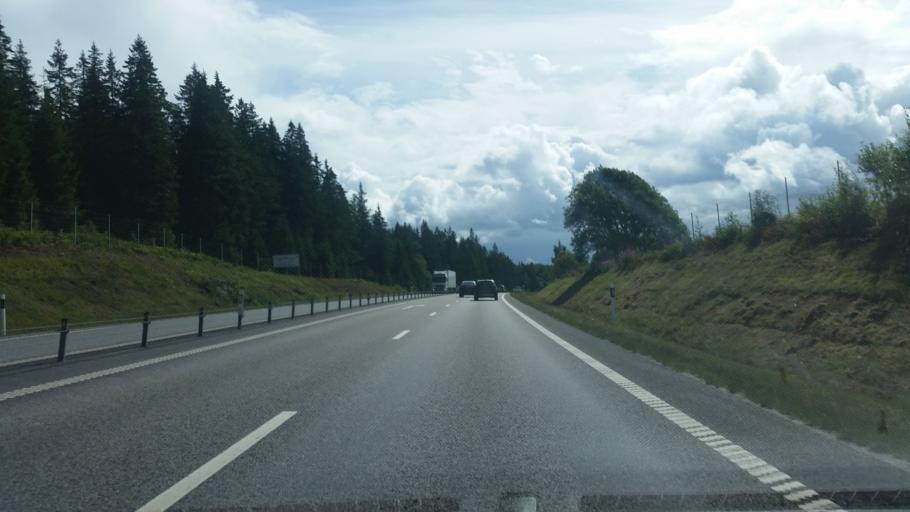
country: SE
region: Joenkoeping
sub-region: Mullsjo Kommun
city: Mullsjoe
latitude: 57.7705
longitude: 13.7153
